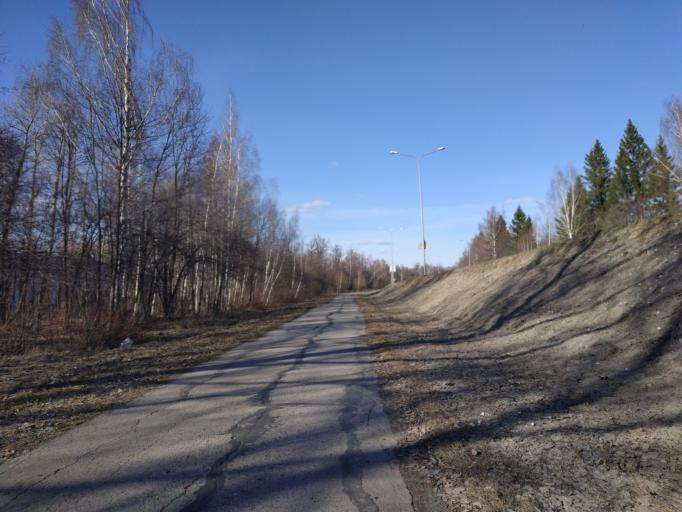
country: RU
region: Chuvashia
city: Ishley
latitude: 56.1223
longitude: 47.0604
